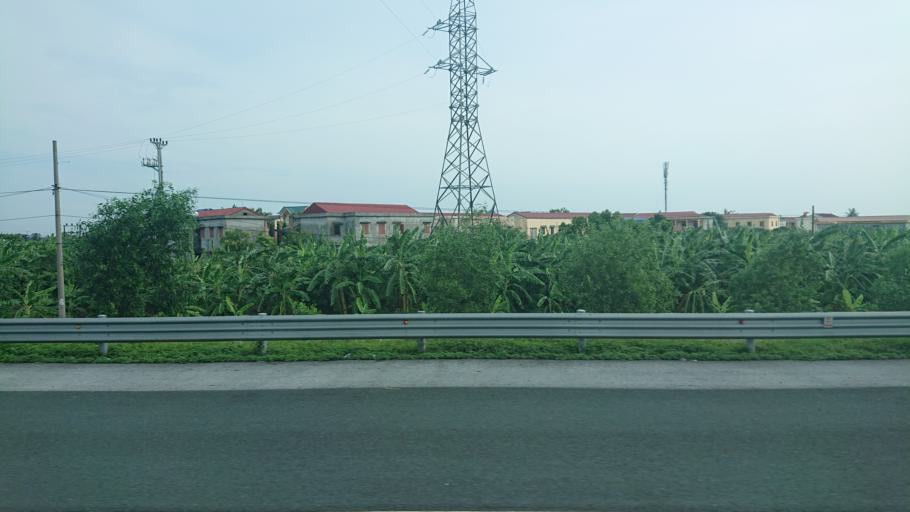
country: VN
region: Hai Phong
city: An Lao
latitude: 20.8138
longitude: 106.4971
